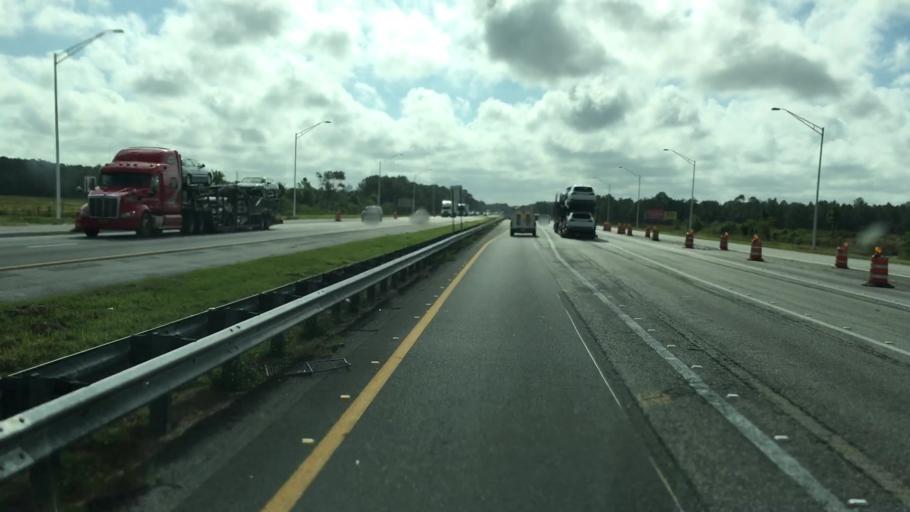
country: US
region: Florida
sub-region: Volusia County
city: South Daytona
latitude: 29.1474
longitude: -81.0712
